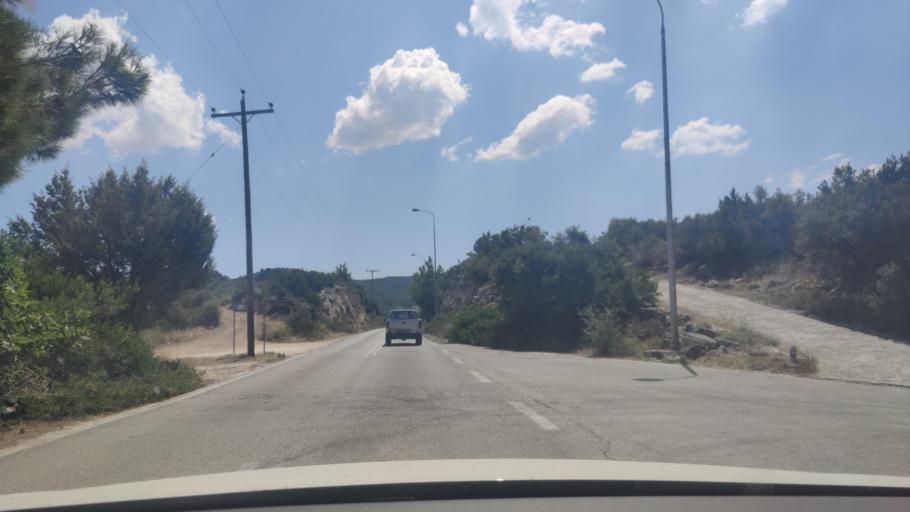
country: GR
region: East Macedonia and Thrace
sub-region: Nomos Kavalas
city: Limenaria
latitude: 40.6414
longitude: 24.5204
